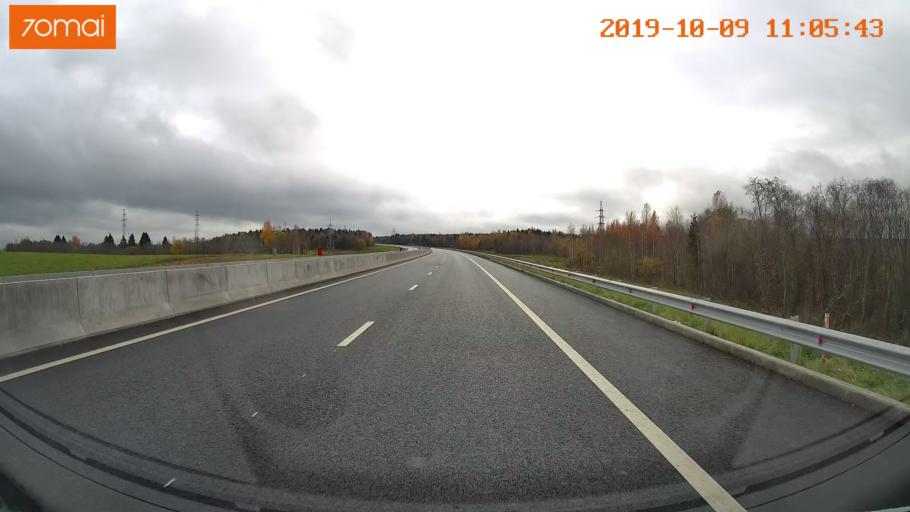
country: RU
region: Vologda
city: Molochnoye
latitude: 59.1960
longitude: 39.7580
